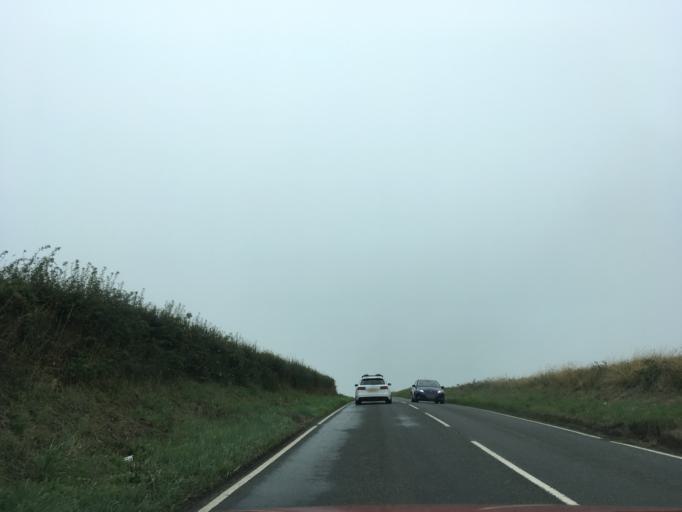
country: GB
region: Wales
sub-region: Pembrokeshire
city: Llanrhian
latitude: 51.8738
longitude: -5.1595
